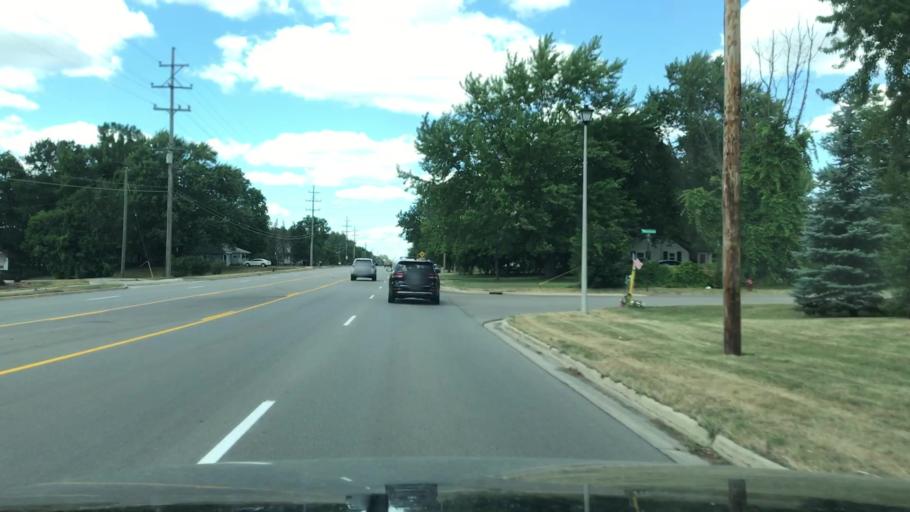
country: US
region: Michigan
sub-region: Kent County
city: Byron Center
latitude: 42.8313
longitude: -85.7228
